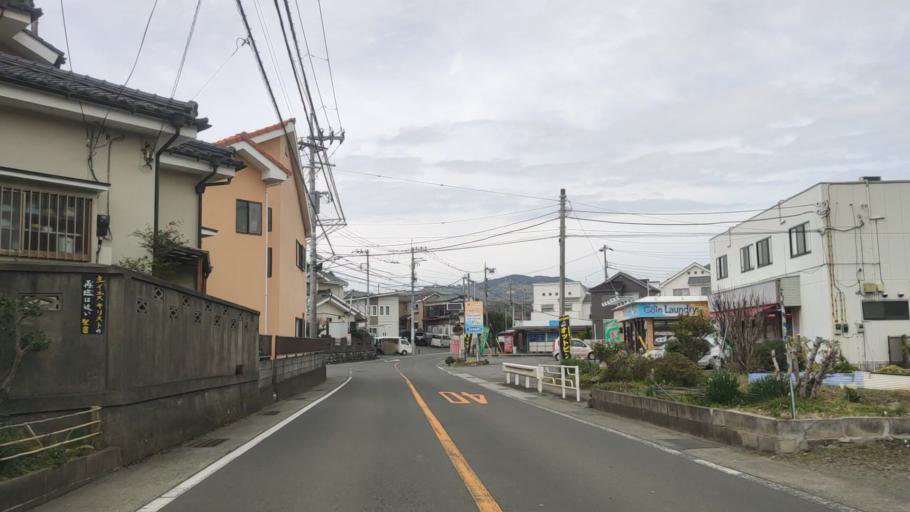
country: JP
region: Kanagawa
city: Ninomiya
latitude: 35.2985
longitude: 139.2311
